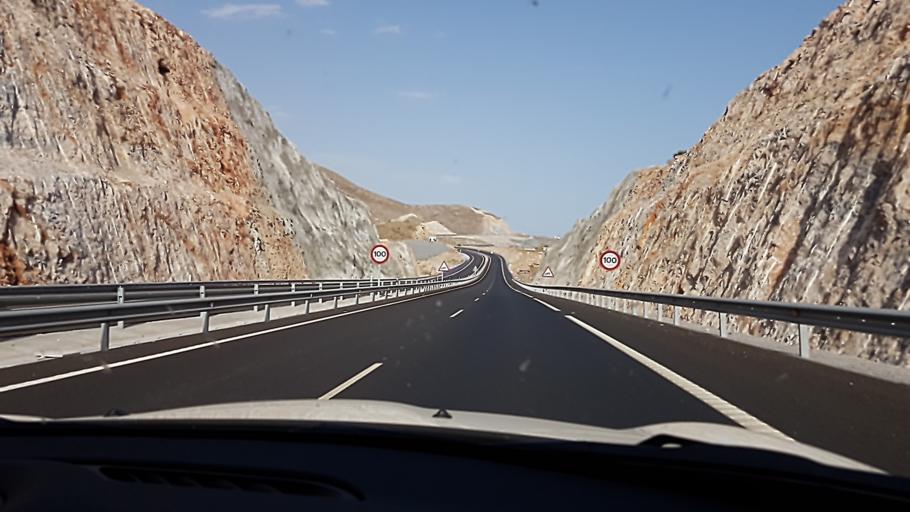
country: ES
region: Andalusia
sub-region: Provincia de Granada
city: Gualchos
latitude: 36.7102
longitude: -3.4078
